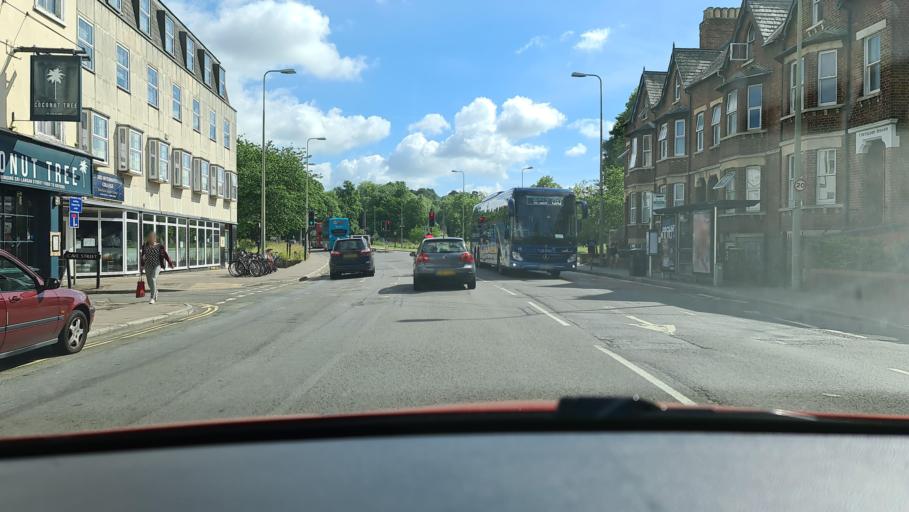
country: GB
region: England
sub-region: Oxfordshire
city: Oxford
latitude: 51.7508
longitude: -1.2389
